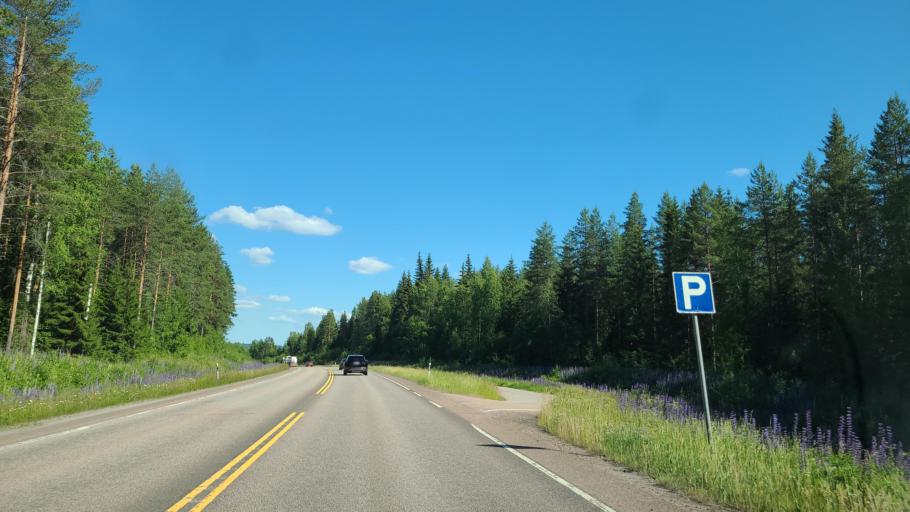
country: FI
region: Central Finland
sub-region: Jyvaeskylae
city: Petaejaevesi
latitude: 62.2676
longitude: 25.4298
